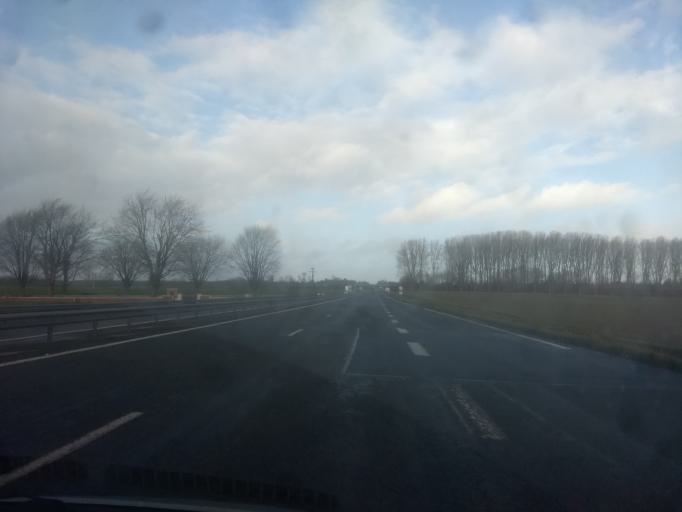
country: FR
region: Nord-Pas-de-Calais
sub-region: Departement du Pas-de-Calais
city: Thelus
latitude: 50.3456
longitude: 2.7847
